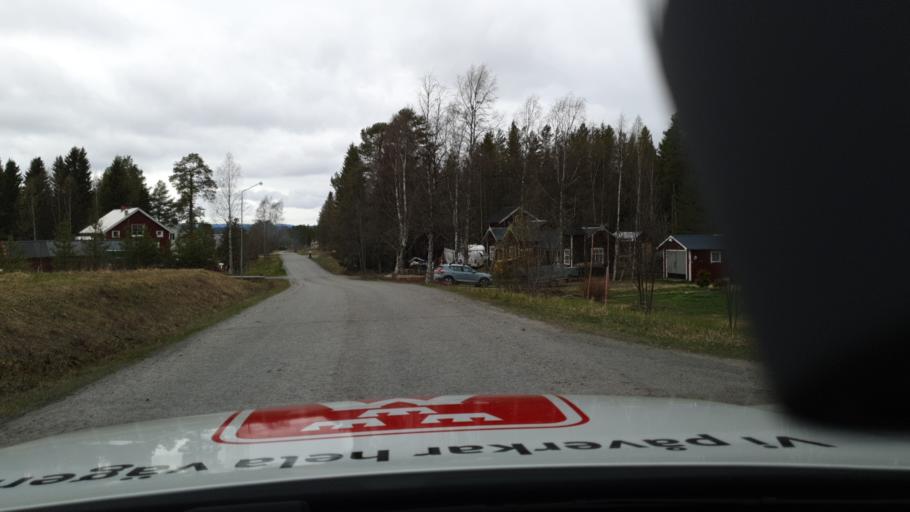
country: SE
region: Jaemtland
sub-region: OEstersunds Kommun
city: Lit
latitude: 63.6084
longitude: 14.7807
